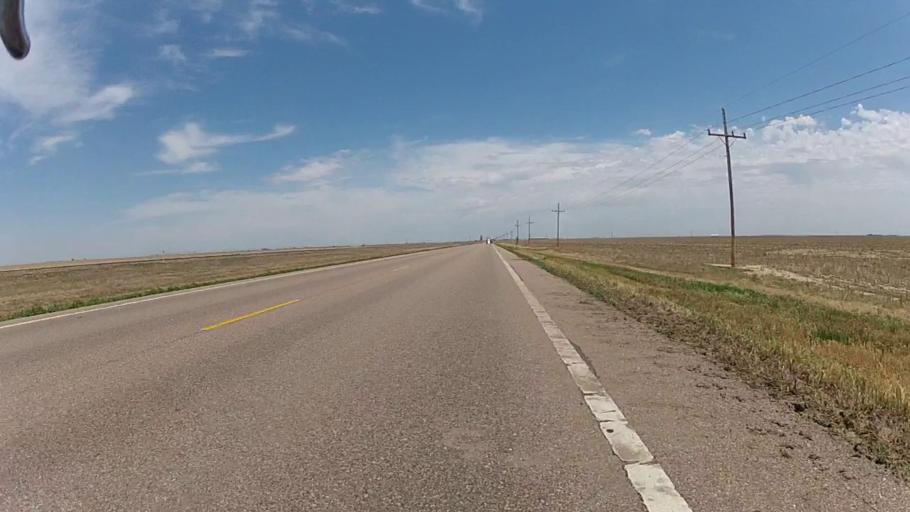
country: US
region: Kansas
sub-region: Haskell County
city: Satanta
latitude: 37.4644
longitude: -100.9121
